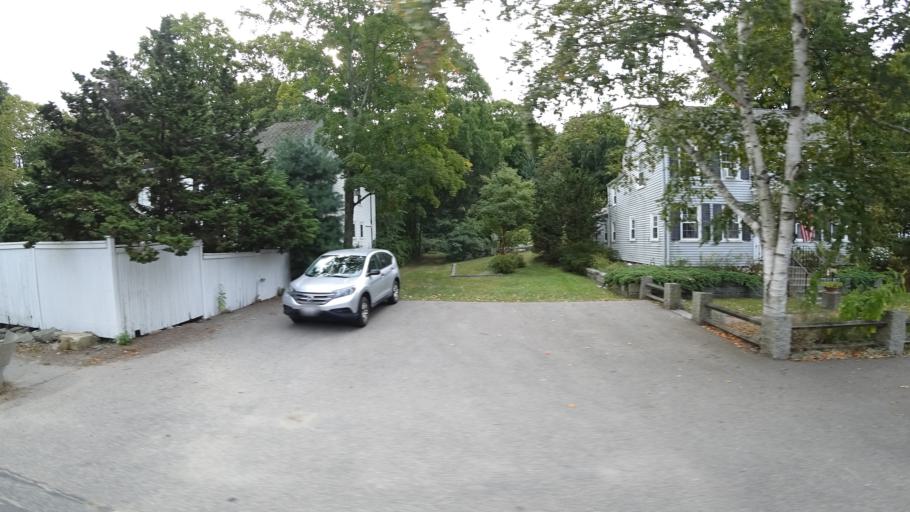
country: US
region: Massachusetts
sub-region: Norfolk County
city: Dedham
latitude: 42.2479
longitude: -71.1916
